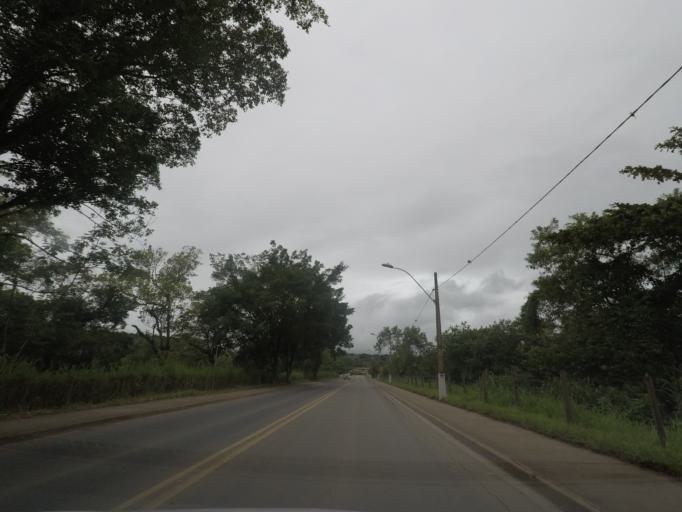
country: BR
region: Sao Paulo
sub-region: Cajati
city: Cajati
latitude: -24.7265
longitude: -48.0984
